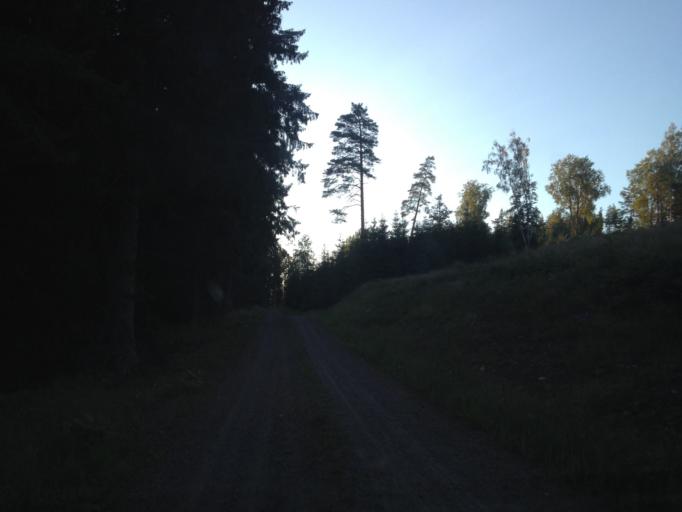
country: SE
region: Kalmar
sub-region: Vasterviks Kommun
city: Overum
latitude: 58.0104
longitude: 16.1215
